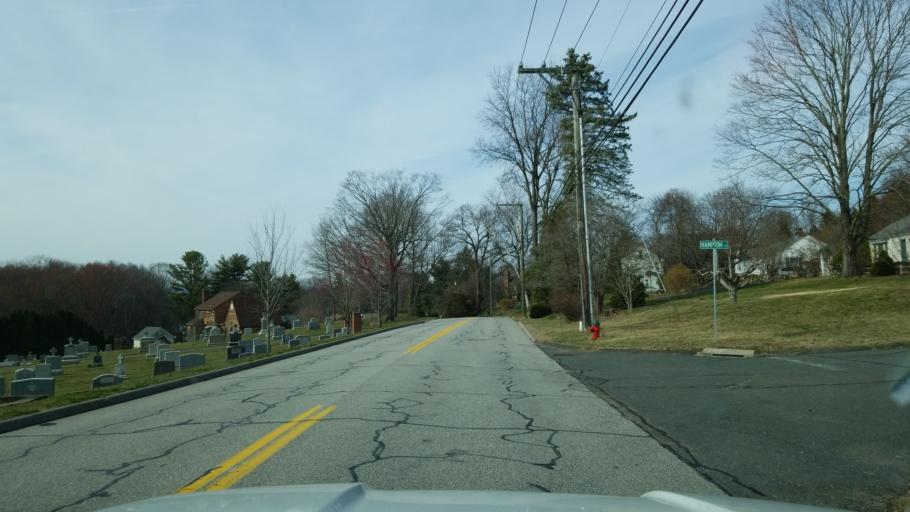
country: US
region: Connecticut
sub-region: Hartford County
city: Glastonbury Center
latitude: 41.6648
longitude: -72.5944
